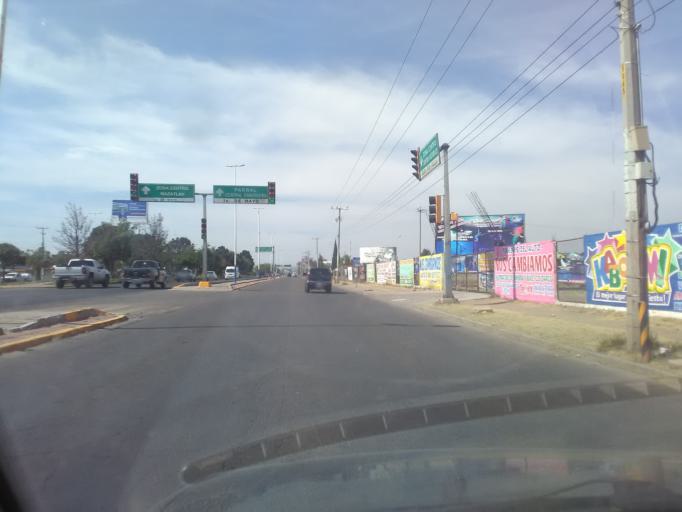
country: MX
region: Durango
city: Victoria de Durango
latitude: 24.0503
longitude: -104.6202
